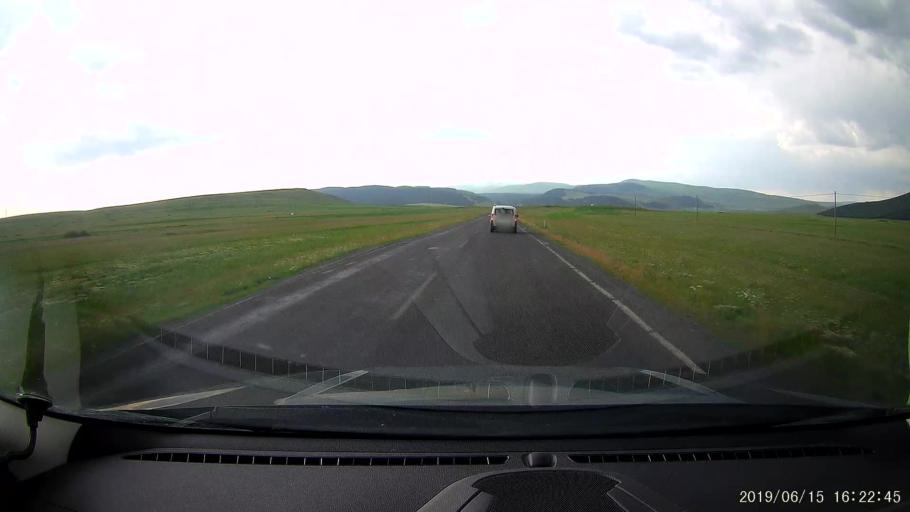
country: TR
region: Ardahan
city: Hanak
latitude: 41.1850
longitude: 42.8542
